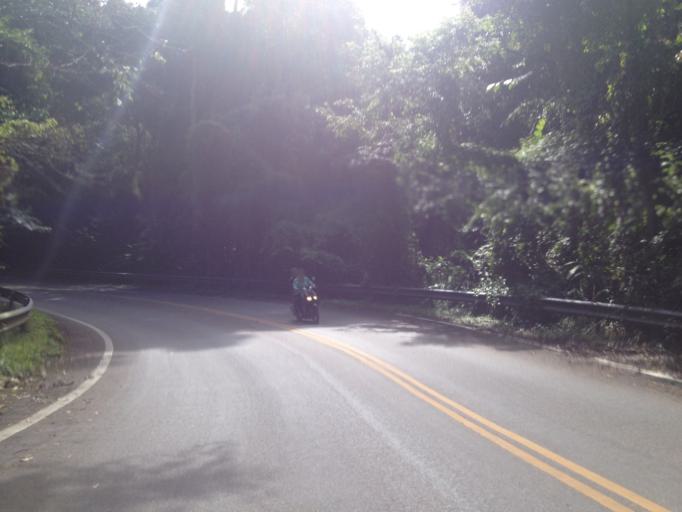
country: TH
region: Chiang Mai
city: Chiang Mai
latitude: 18.8078
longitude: 98.9106
